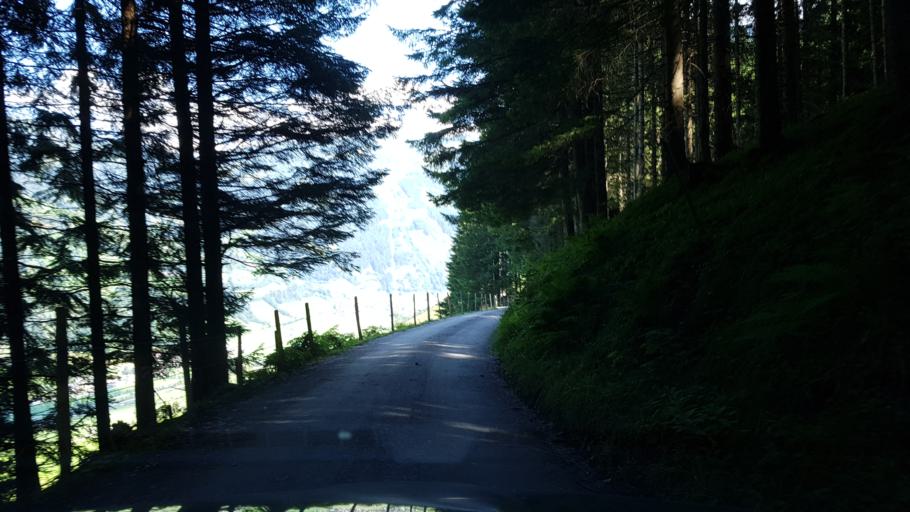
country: AT
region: Salzburg
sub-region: Politischer Bezirk Sankt Johann im Pongau
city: Dorfgastein
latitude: 47.2530
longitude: 13.0737
